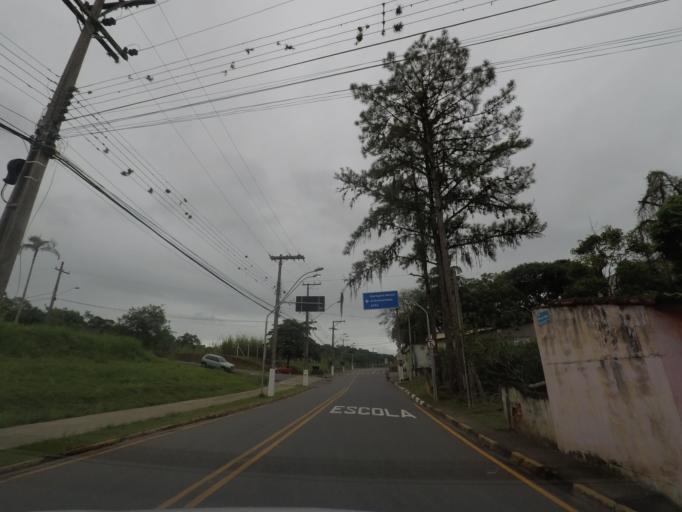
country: BR
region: Sao Paulo
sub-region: Cajati
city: Cajati
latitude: -24.7216
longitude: -48.1023
